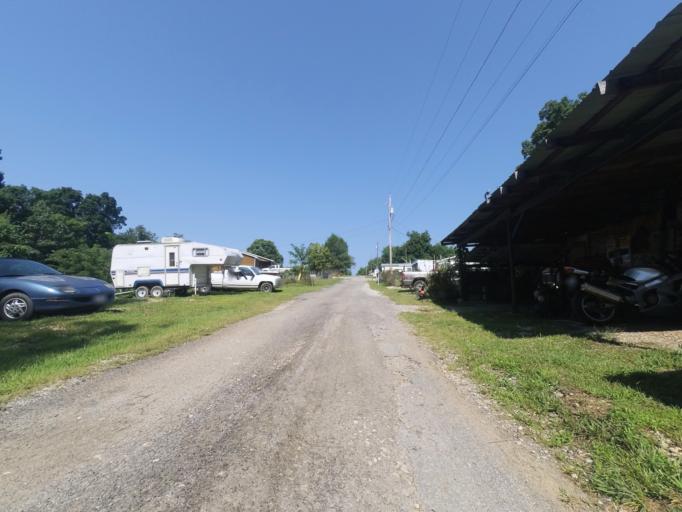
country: US
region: West Virginia
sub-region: Cabell County
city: Huntington
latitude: 38.4329
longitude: -82.4436
